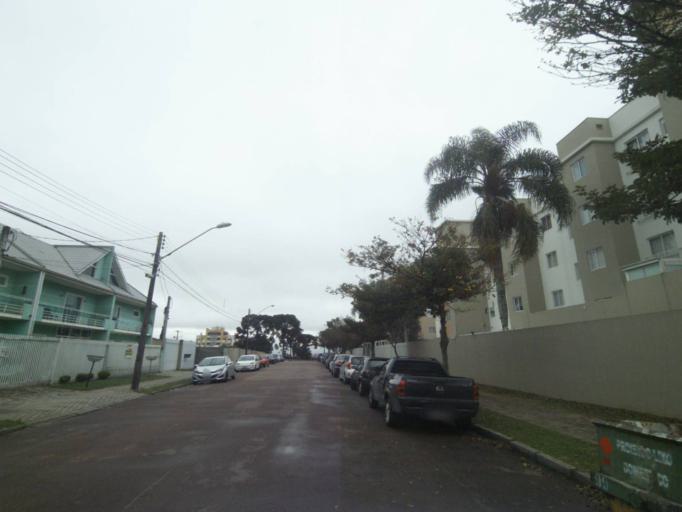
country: BR
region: Parana
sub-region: Curitiba
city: Curitiba
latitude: -25.4996
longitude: -49.3009
